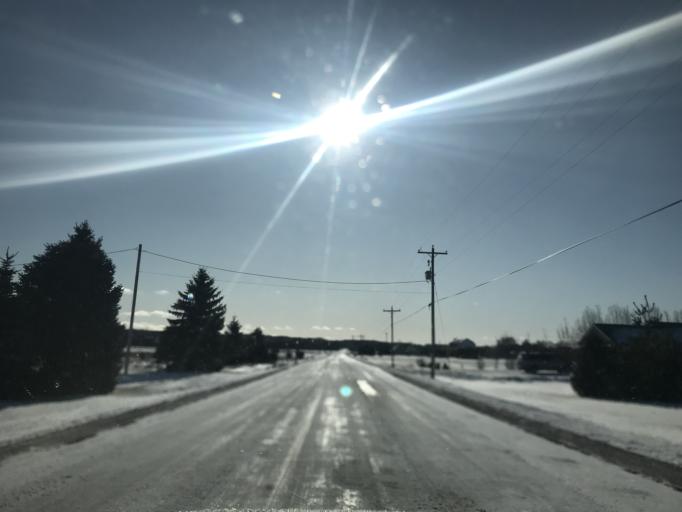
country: US
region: Wisconsin
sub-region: Door County
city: Sturgeon Bay
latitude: 44.8382
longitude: -87.5040
